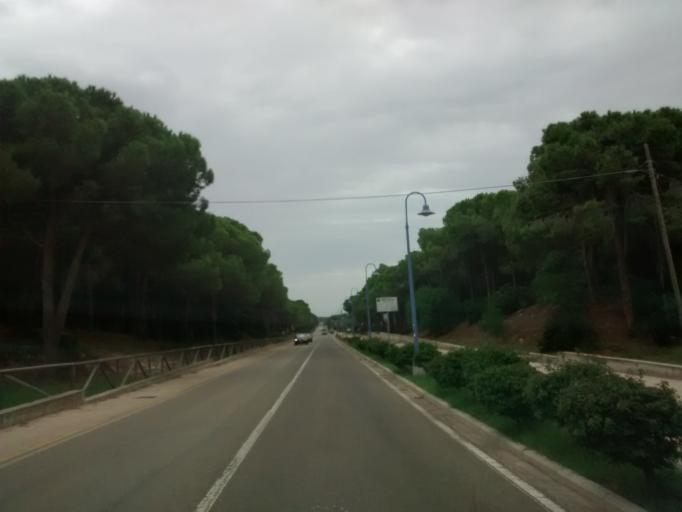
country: IT
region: Sardinia
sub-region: Provincia di Cagliari
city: Villasimius
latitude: 39.1256
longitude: 9.5153
